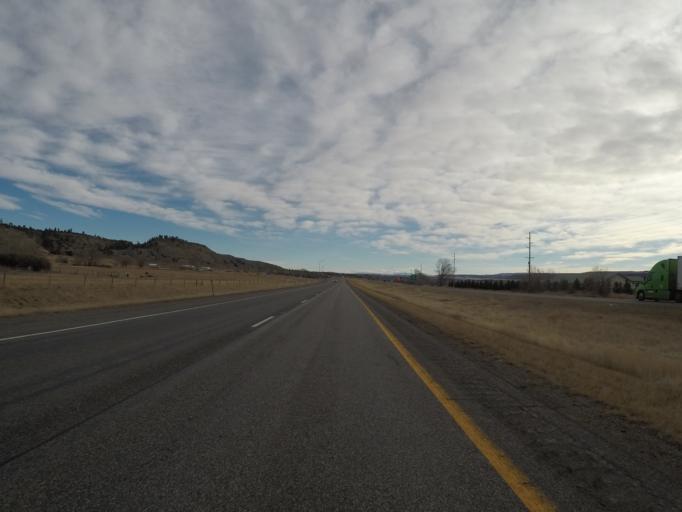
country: US
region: Montana
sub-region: Stillwater County
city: Columbus
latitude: 45.6507
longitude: -109.2558
